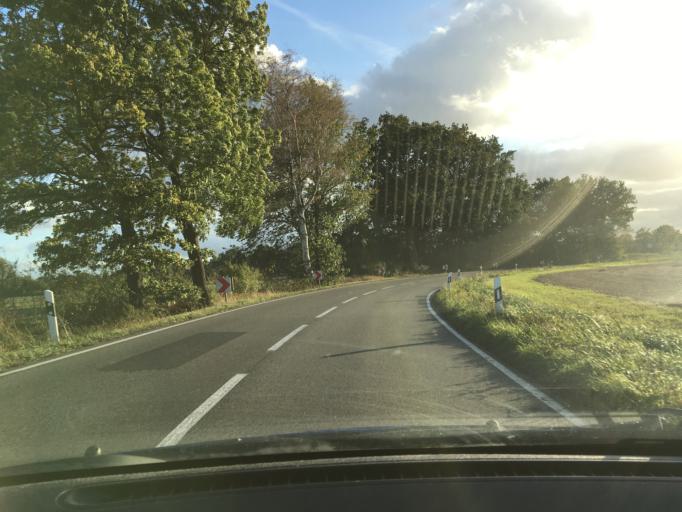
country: DE
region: Lower Saxony
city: Hittbergen
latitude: 53.3320
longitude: 10.5990
